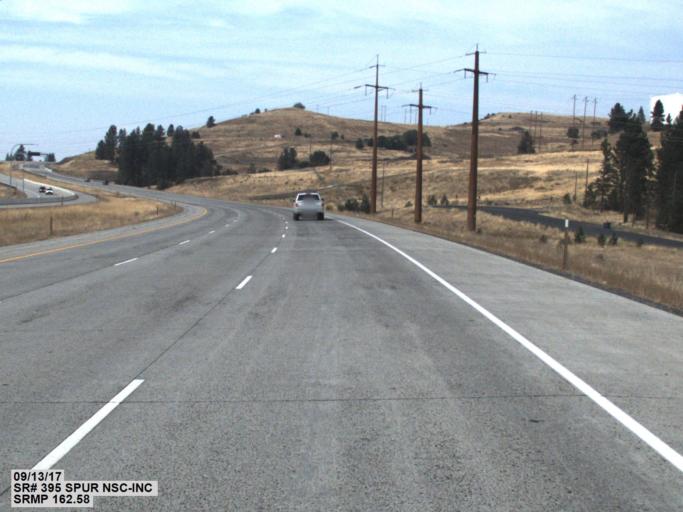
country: US
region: Washington
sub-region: Spokane County
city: Mead
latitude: 47.7583
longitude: -117.3580
